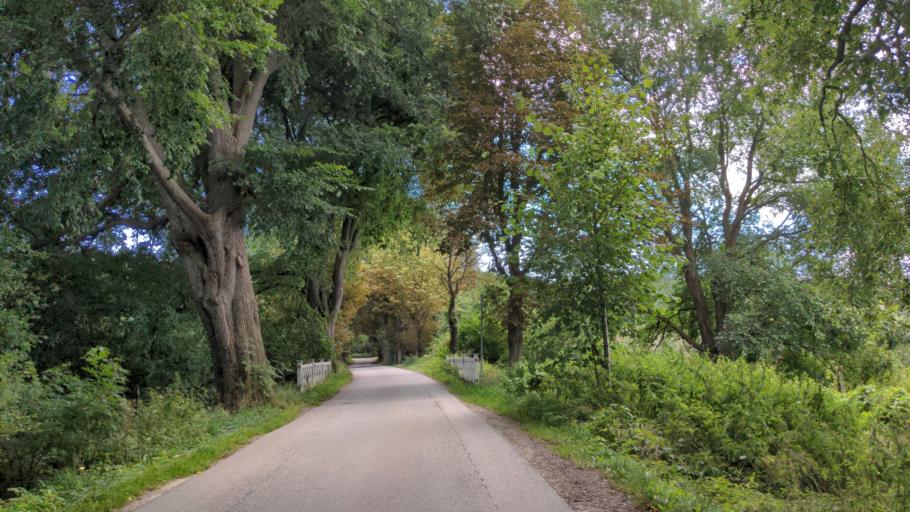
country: DE
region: Schleswig-Holstein
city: Kasseedorf
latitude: 54.1616
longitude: 10.6891
